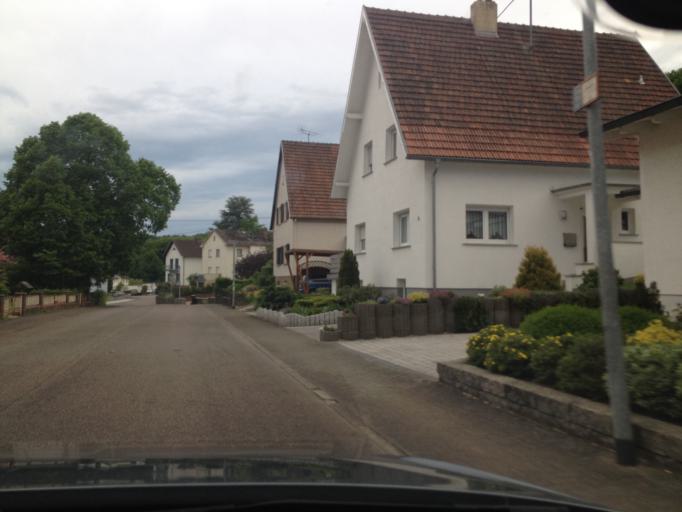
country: DE
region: Saarland
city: Spiesen-Elversberg
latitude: 49.3289
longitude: 7.1451
